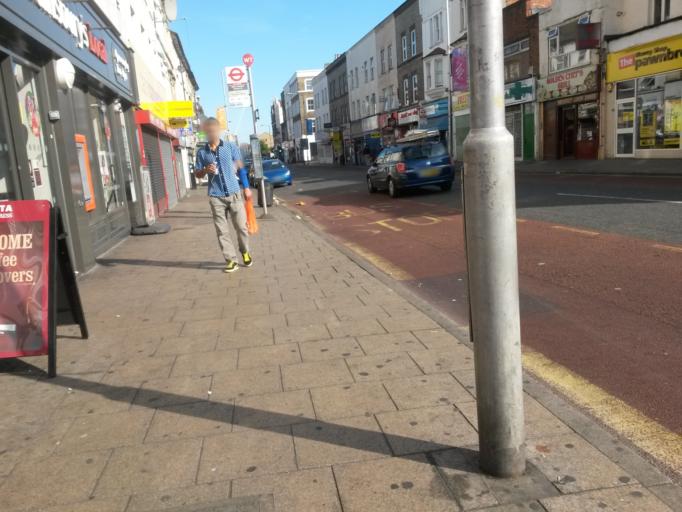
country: GB
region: England
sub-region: Greater London
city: Croydon
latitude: 51.3785
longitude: -0.1030
